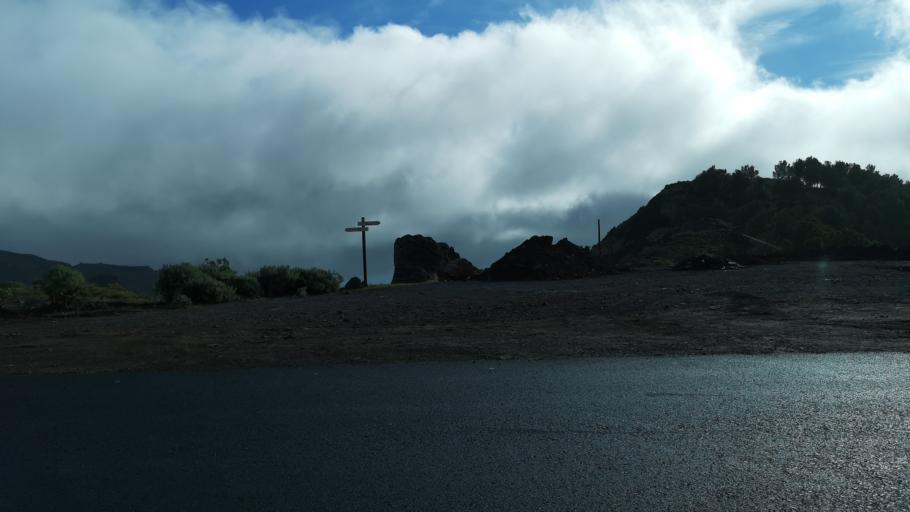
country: ES
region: Canary Islands
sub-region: Provincia de Santa Cruz de Tenerife
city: Alajero
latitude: 28.0886
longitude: -17.1997
